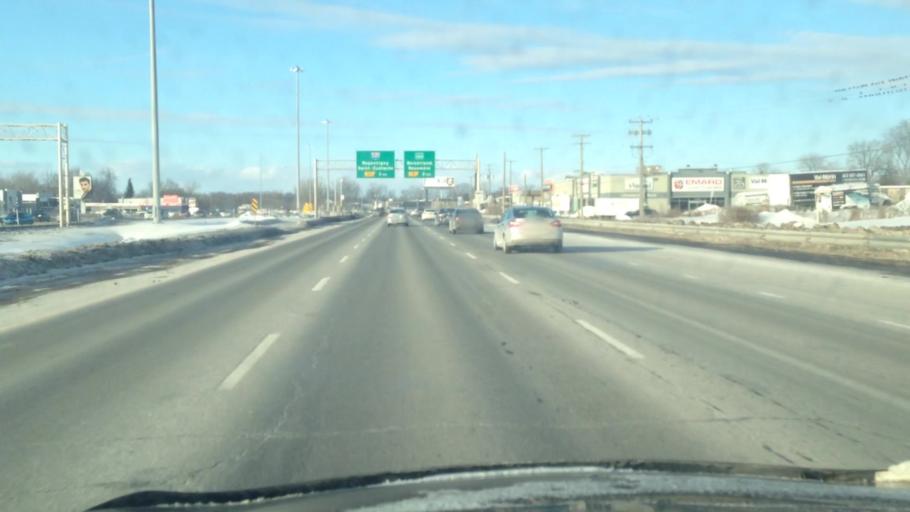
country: CA
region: Quebec
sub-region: Laurentides
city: Boisbriand
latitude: 45.6012
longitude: -73.8047
